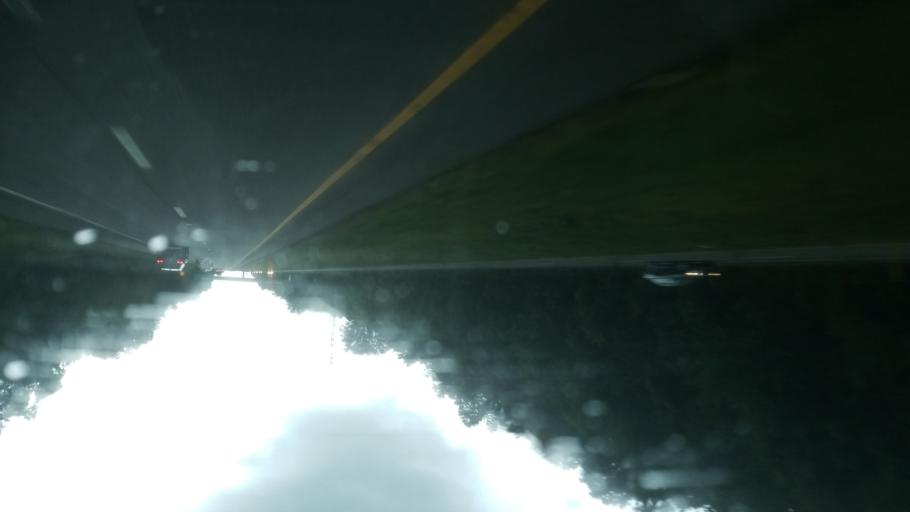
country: US
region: Ohio
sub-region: Geauga County
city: Bainbridge
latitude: 41.3850
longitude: -81.3169
